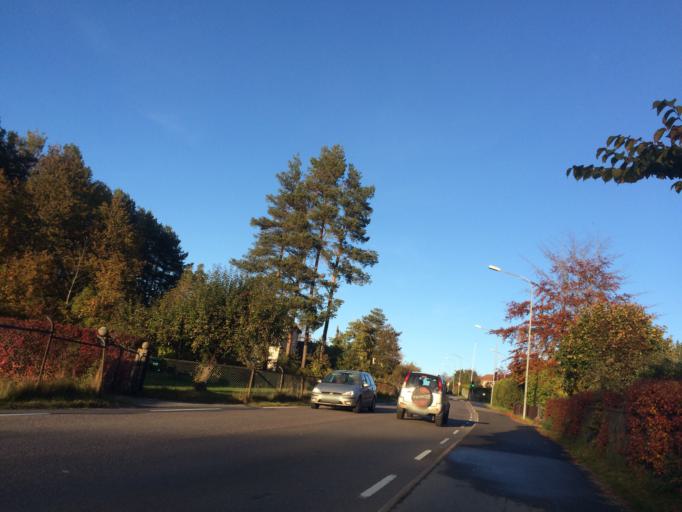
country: NO
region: Akershus
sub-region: Ski
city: Ski
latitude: 59.7197
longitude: 10.8447
